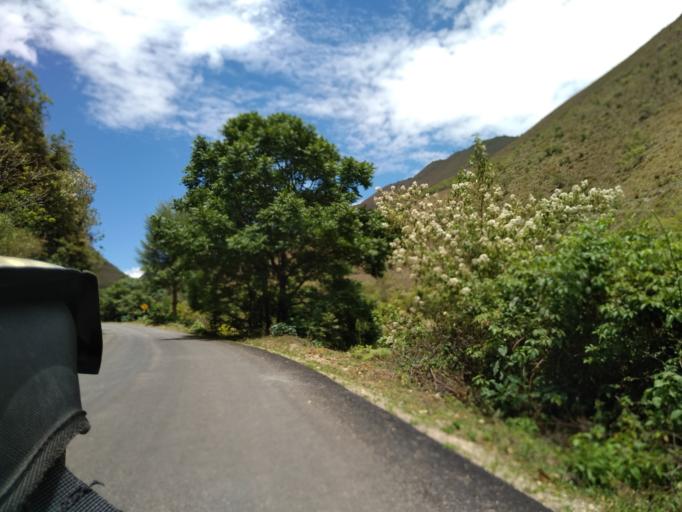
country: PE
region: Amazonas
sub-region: Provincia de Chachapoyas
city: Montevideo
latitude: -6.6600
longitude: -77.7993
